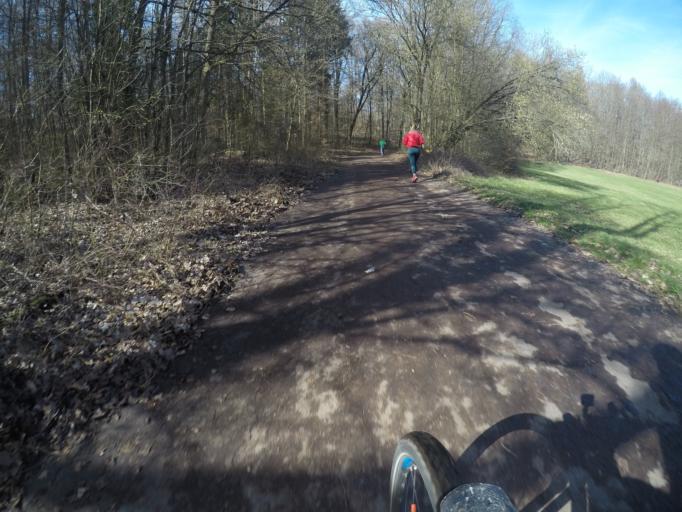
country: DE
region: Baden-Wuerttemberg
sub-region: Regierungsbezirk Stuttgart
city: Korntal
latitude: 48.7998
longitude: 9.1130
